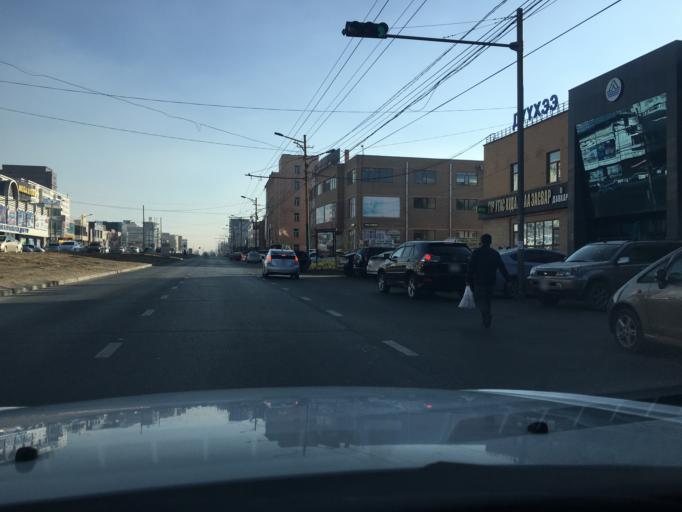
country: MN
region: Ulaanbaatar
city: Ulaanbaatar
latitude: 47.9224
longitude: 106.8693
